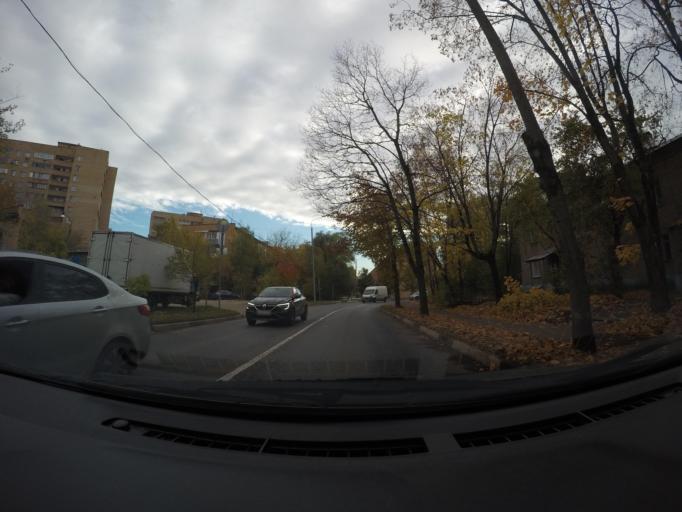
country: RU
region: Moskovskaya
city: Mytishchi
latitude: 55.9175
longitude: 37.7429
